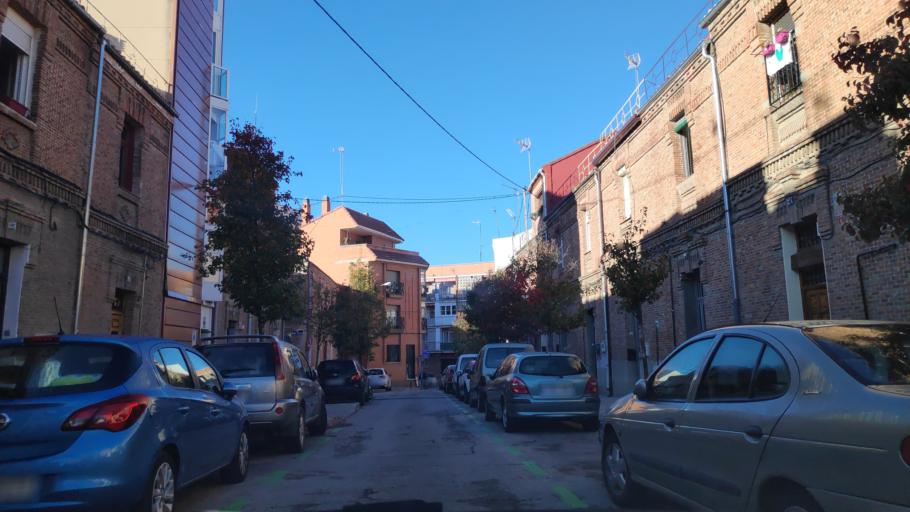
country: ES
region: Madrid
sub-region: Provincia de Madrid
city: Chamberi
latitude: 40.4506
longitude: -3.7066
